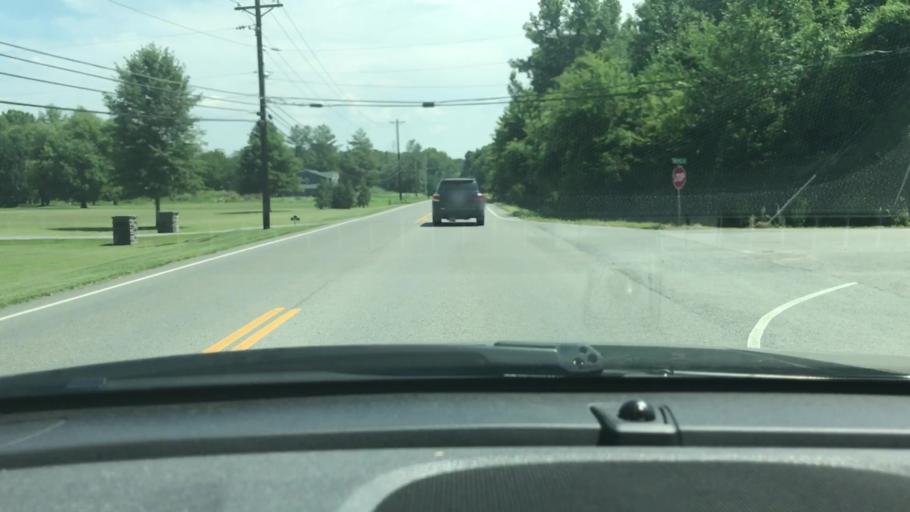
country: US
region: Tennessee
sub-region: Sumner County
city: Shackle Island
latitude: 36.3630
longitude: -86.6114
